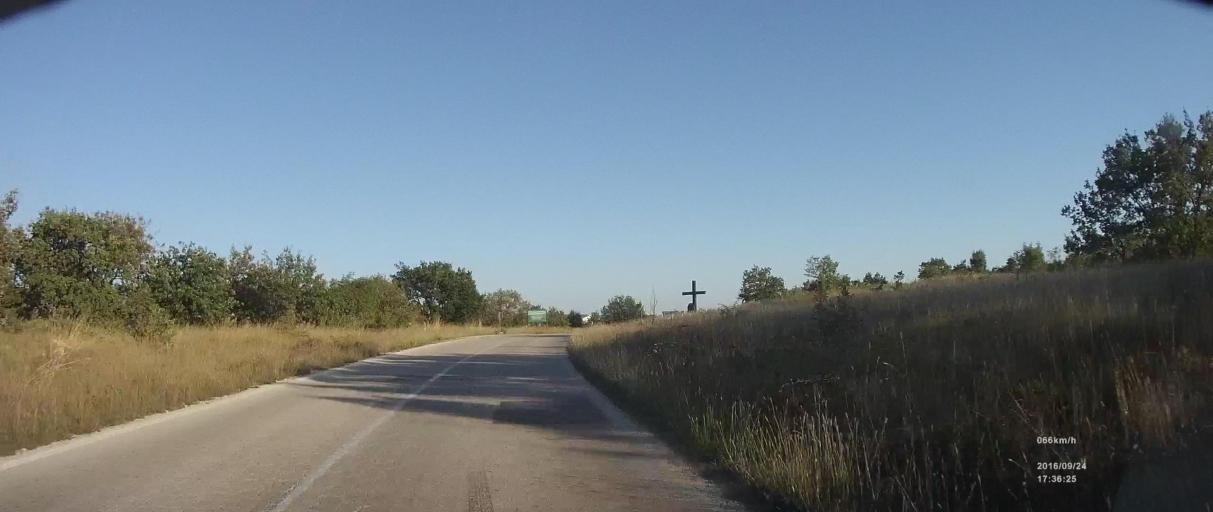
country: HR
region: Zadarska
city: Posedarje
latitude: 44.1552
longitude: 15.4757
